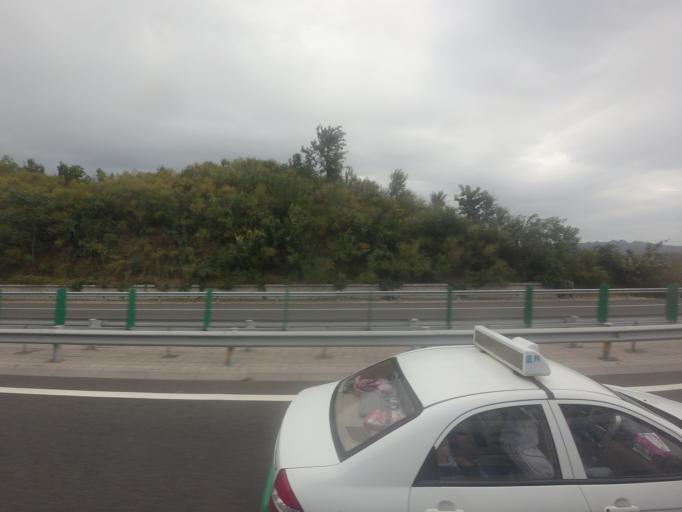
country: CN
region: Beijing
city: Dachengzi
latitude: 40.4161
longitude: 117.1438
